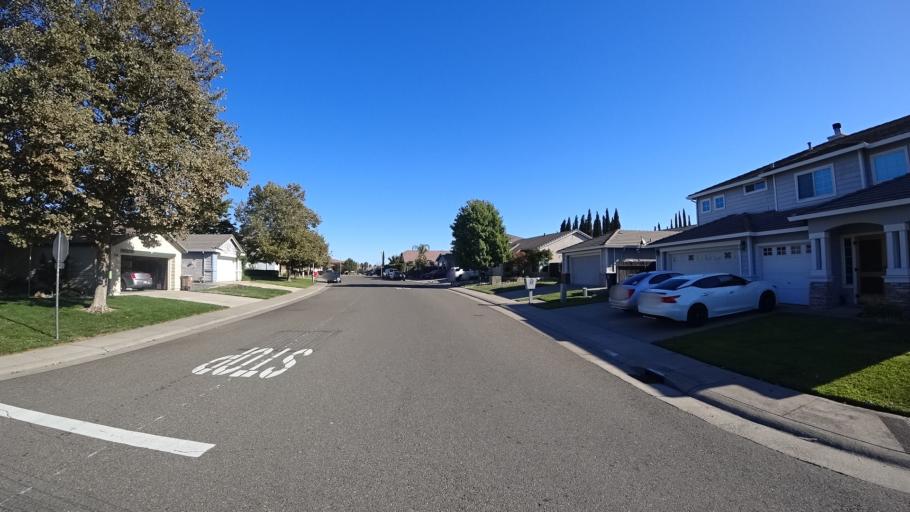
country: US
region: California
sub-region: Sacramento County
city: Vineyard
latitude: 38.4429
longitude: -121.3677
